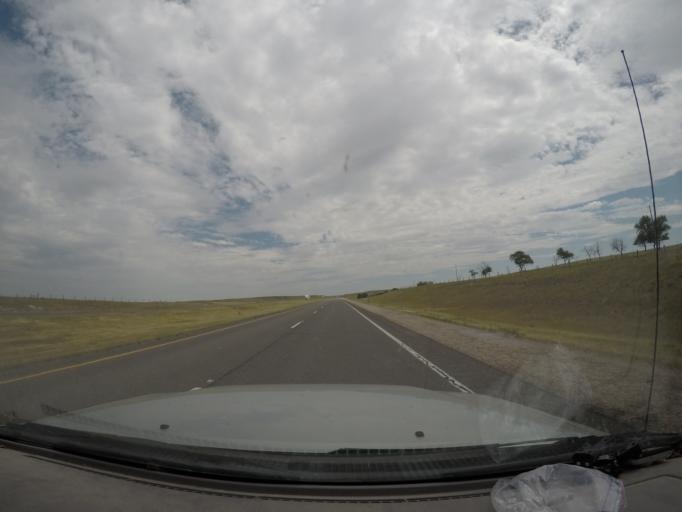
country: US
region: Wyoming
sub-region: Laramie County
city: Pine Bluffs
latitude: 41.1919
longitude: -103.9399
